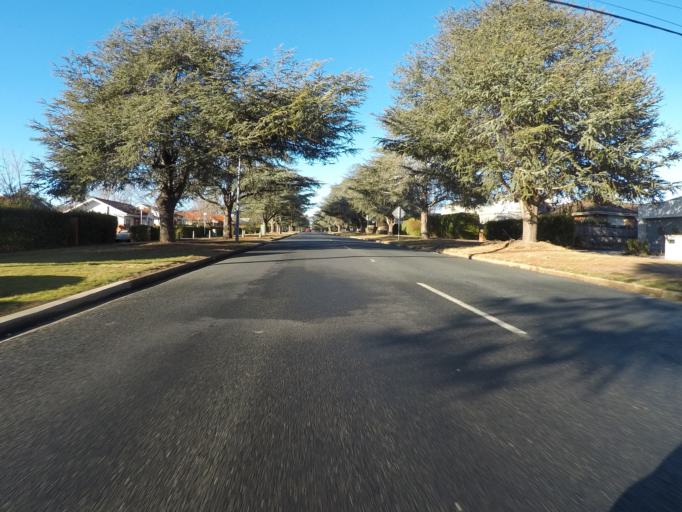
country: AU
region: Australian Capital Territory
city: Forrest
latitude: -35.3081
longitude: 149.0983
